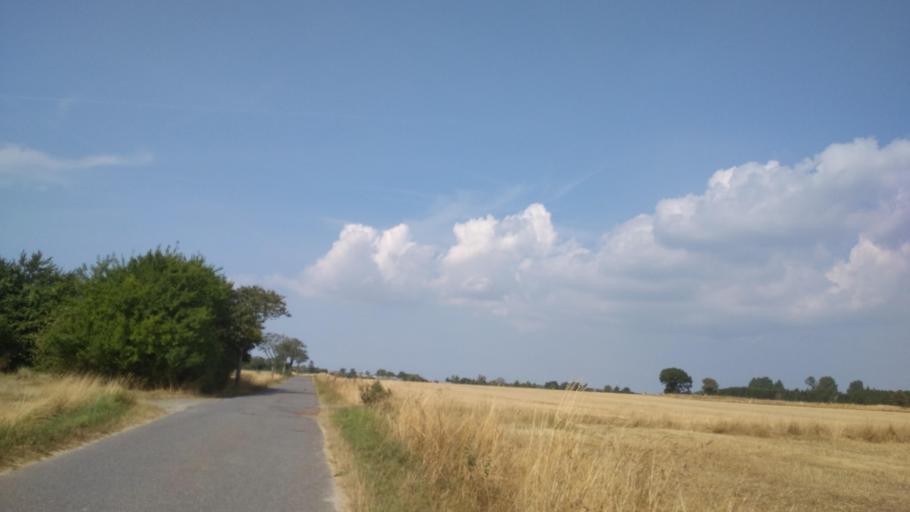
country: DK
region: Capital Region
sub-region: Bornholm Kommune
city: Akirkeby
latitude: 55.0647
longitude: 14.9357
